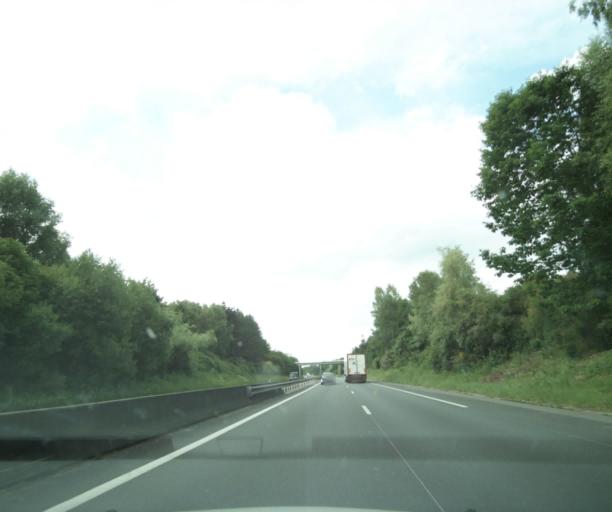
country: FR
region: Centre
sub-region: Departement du Cher
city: Vierzon
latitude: 47.2213
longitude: 2.1100
